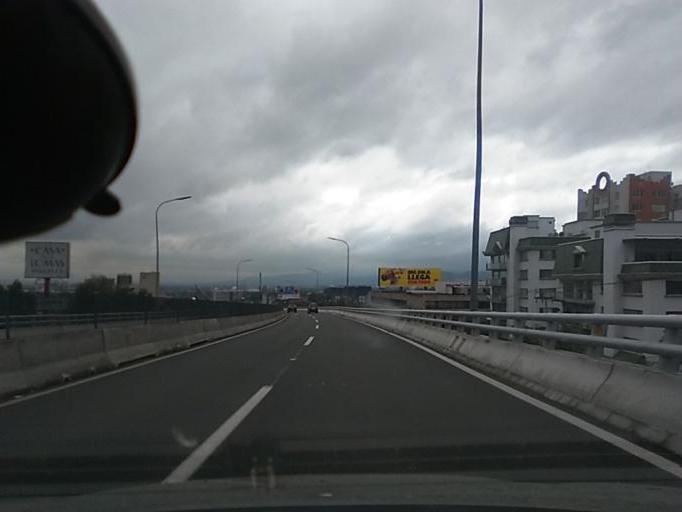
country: MX
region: Mexico City
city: Tlalpan
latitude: 19.3030
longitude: -99.1983
